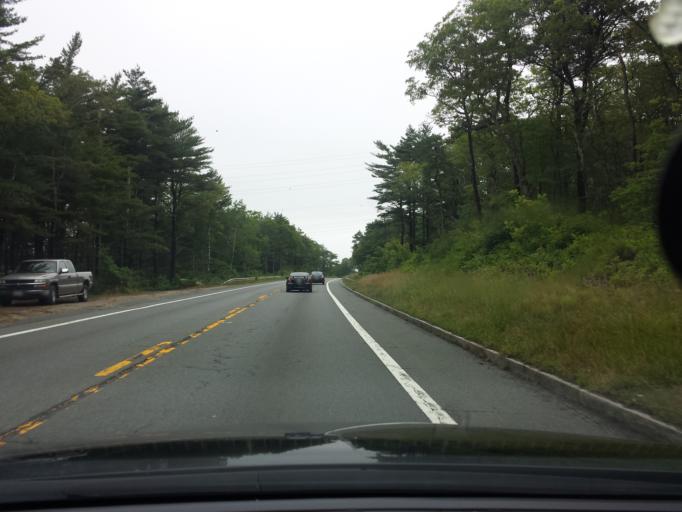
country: US
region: Massachusetts
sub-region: Barnstable County
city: Sagamore
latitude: 41.7650
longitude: -70.5652
